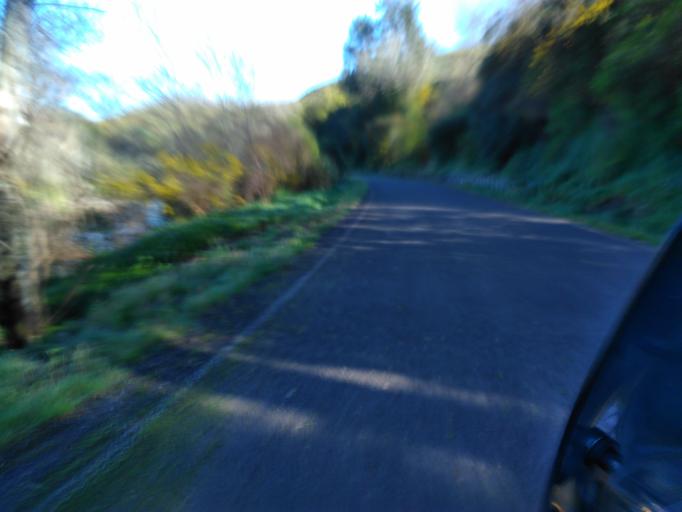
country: NZ
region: Gisborne
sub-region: Gisborne District
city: Gisborne
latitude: -38.4325
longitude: 177.7428
